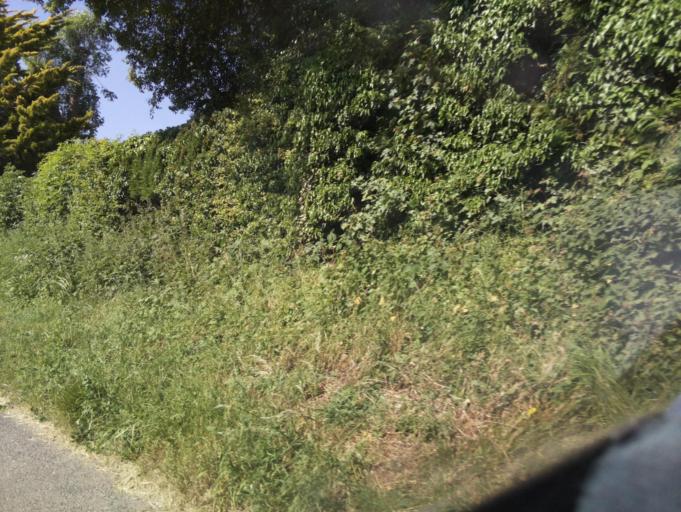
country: GB
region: England
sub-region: Hampshire
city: Abbotts Ann
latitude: 51.2447
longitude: -1.5713
